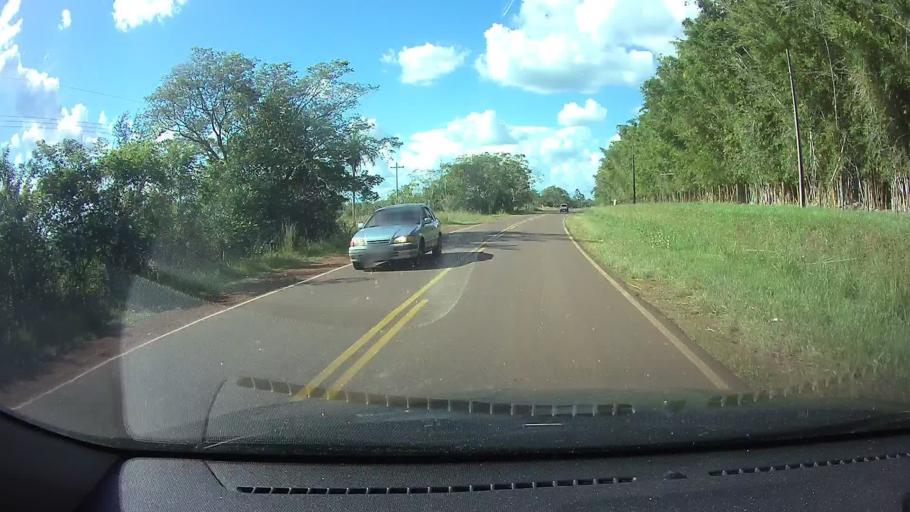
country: PY
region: Cordillera
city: Itacurubi de la Cordillera
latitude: -25.4744
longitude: -56.8812
